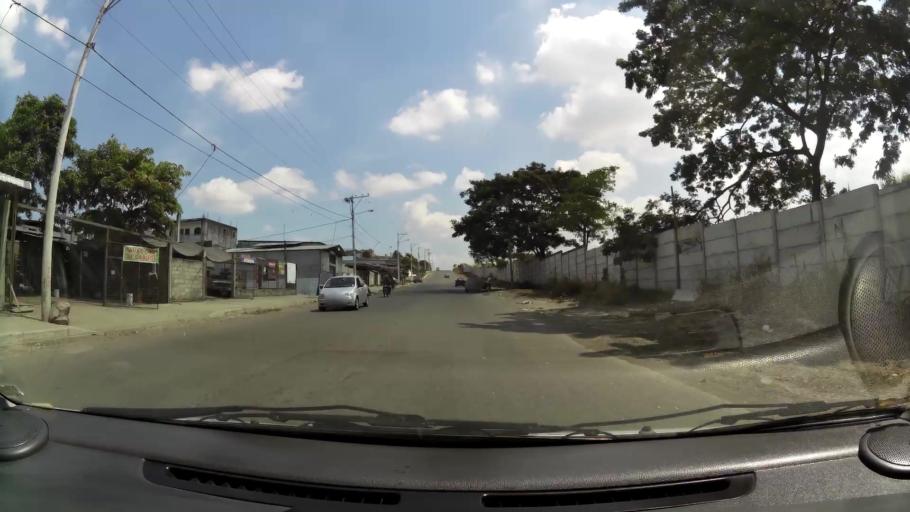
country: EC
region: Guayas
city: Eloy Alfaro
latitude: -2.1133
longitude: -79.9169
